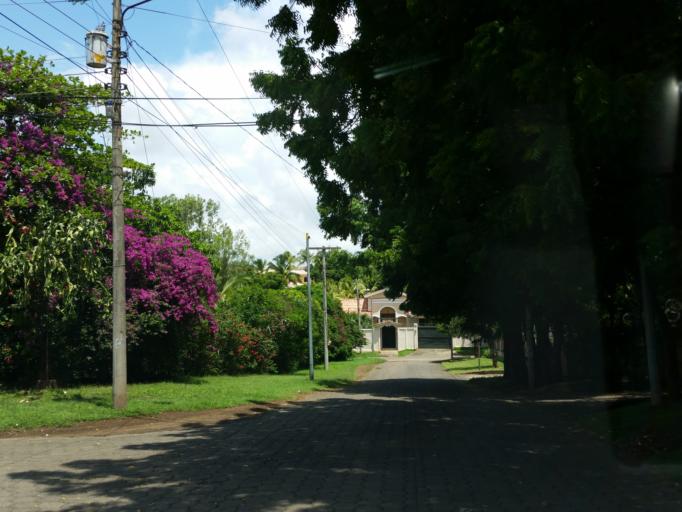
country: NI
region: Managua
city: Managua
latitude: 12.1002
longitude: -86.2398
